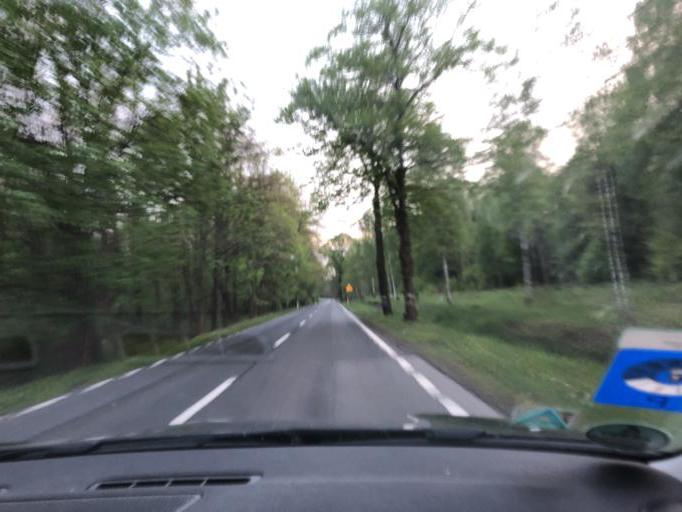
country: PL
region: Lubusz
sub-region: Powiat zarski
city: Trzebiel
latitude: 51.6199
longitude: 14.7951
